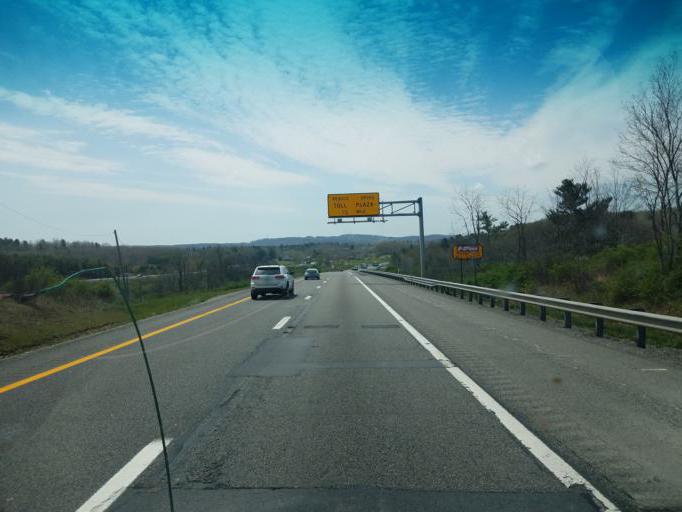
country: US
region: West Virginia
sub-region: Raleigh County
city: Shady Spring
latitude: 37.6389
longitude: -81.1115
